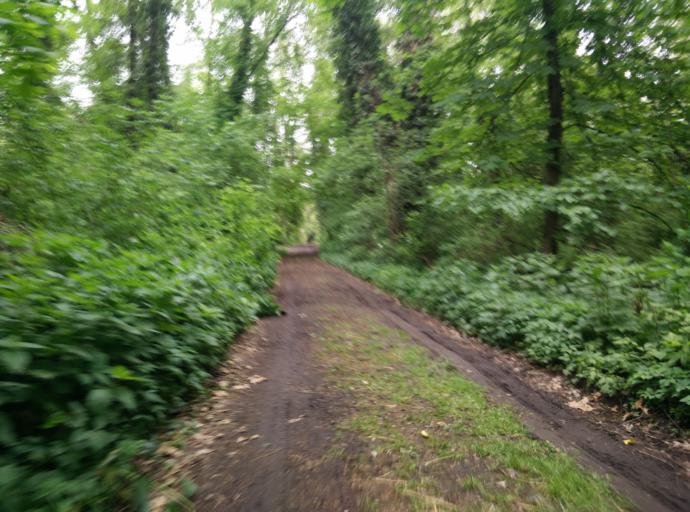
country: HU
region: Pest
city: Fot
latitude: 47.6064
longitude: 19.1873
